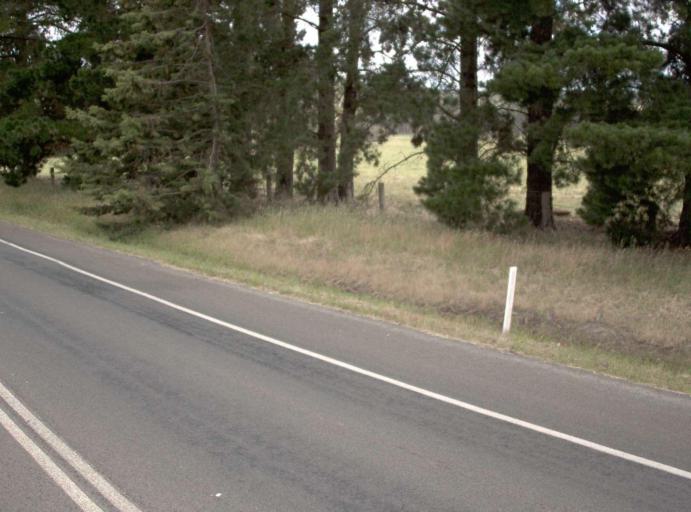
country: AU
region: Victoria
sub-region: Latrobe
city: Morwell
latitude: -38.1690
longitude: 146.4126
